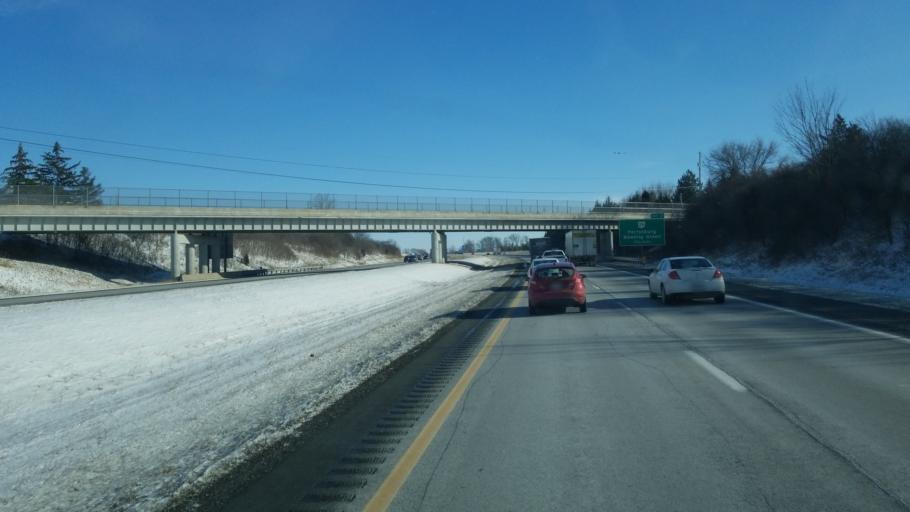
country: US
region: Ohio
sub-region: Lucas County
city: Maumee
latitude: 41.5379
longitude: -83.6760
